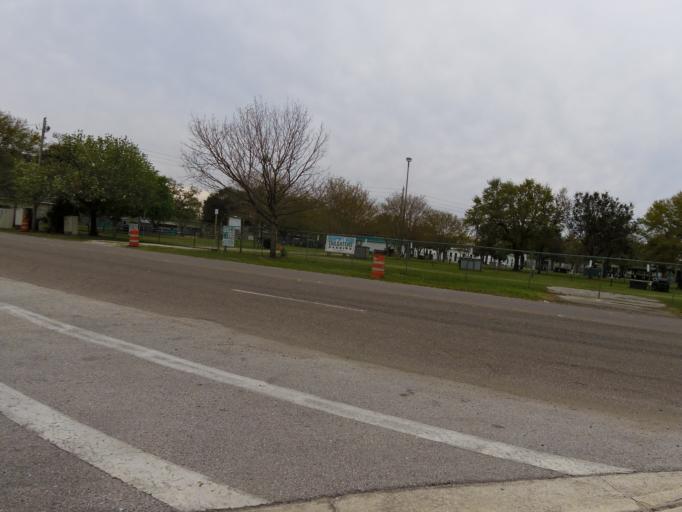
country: US
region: Florida
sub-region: Duval County
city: Jacksonville
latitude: 30.3220
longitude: -81.6331
